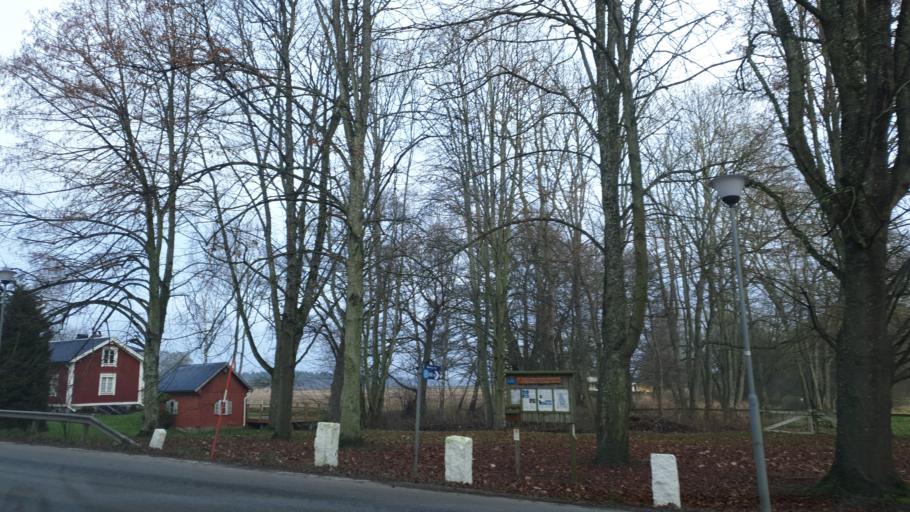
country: SE
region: Blekinge
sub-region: Karlshamns Kommun
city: Morrum
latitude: 56.1636
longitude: 14.7507
